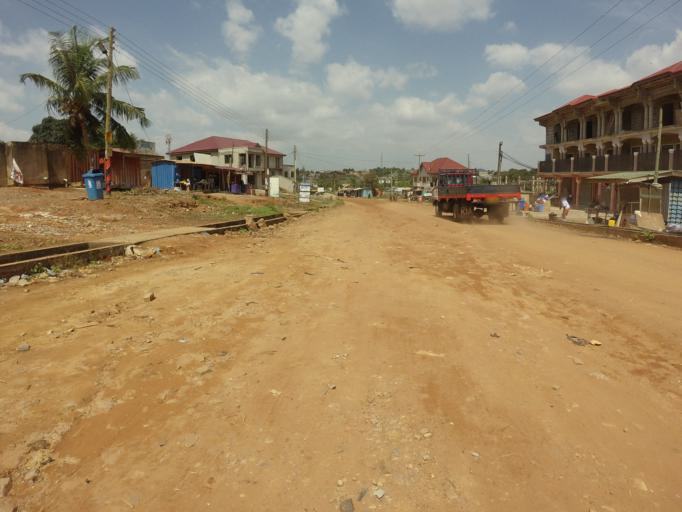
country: GH
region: Greater Accra
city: Gbawe
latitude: 5.6207
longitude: -0.3064
